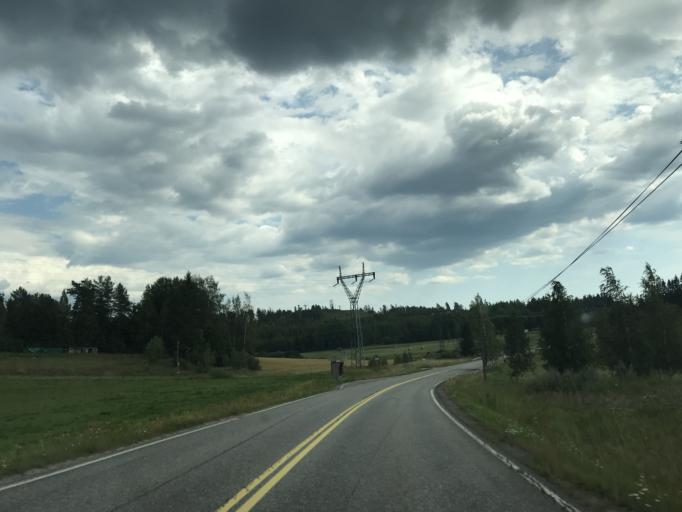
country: FI
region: Uusimaa
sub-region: Helsinki
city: Vihti
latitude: 60.3821
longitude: 24.3541
